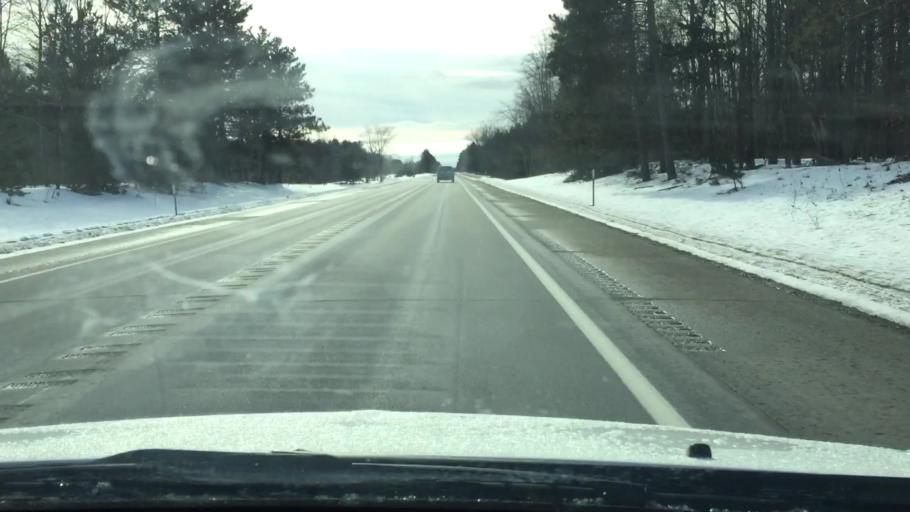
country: US
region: Michigan
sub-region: Kalkaska County
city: Kalkaska
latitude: 44.6923
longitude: -85.2138
